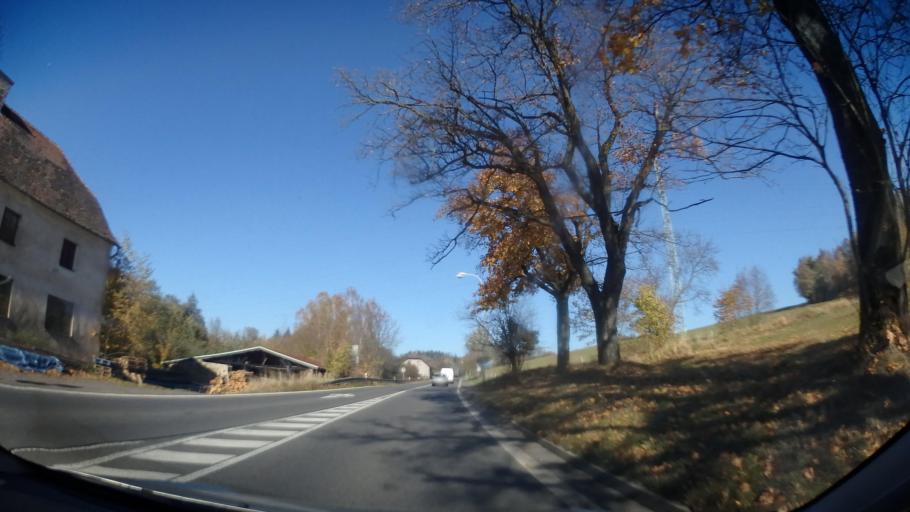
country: CZ
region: Pardubicky
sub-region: Okres Chrudim
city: Nasavrky
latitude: 49.7905
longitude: 15.8123
